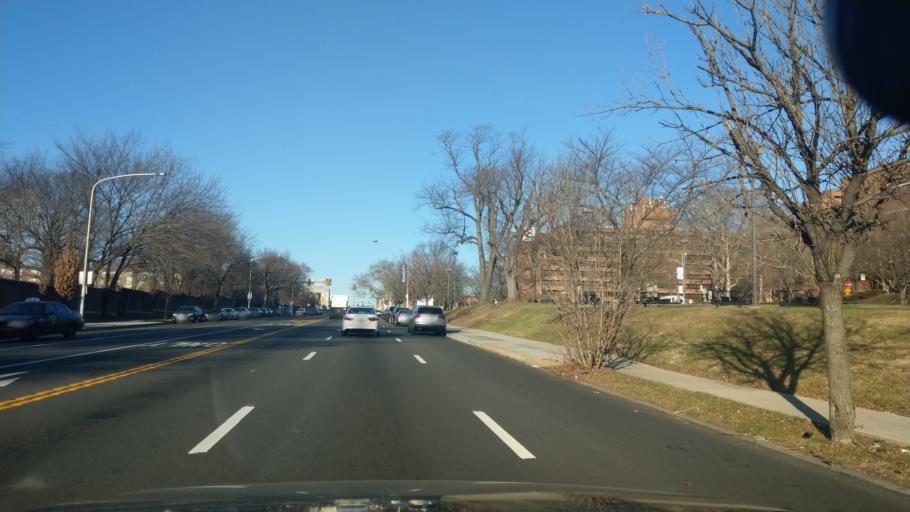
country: US
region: Pennsylvania
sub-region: Montgomery County
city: Wyncote
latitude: 40.0355
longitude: -75.1454
